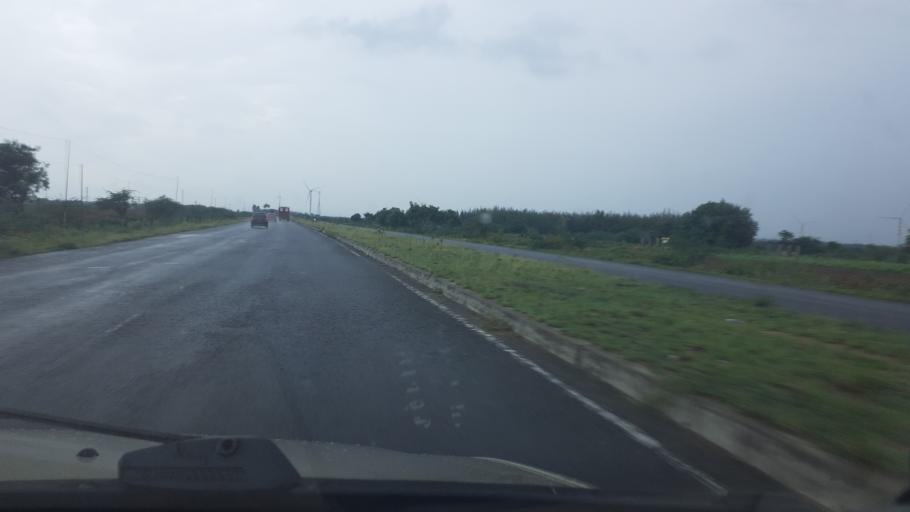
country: IN
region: Tamil Nadu
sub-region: Thoothukkudi
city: Kayattar
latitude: 9.0136
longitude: 77.7843
